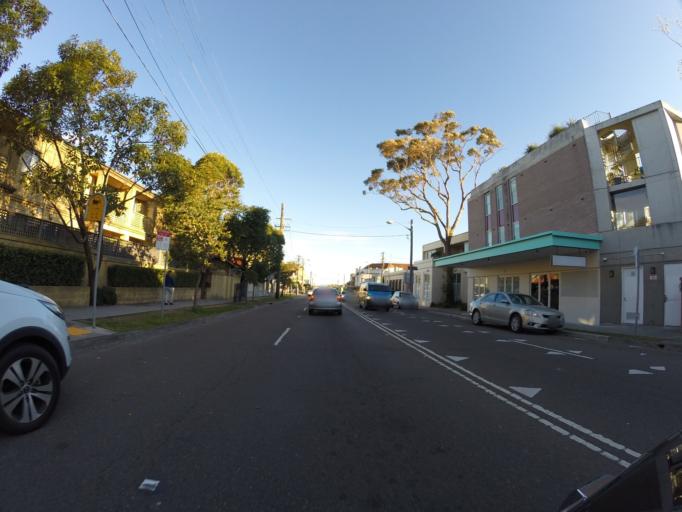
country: AU
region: New South Wales
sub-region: Waverley
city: Bondi Junction
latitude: -33.8994
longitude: 151.2538
